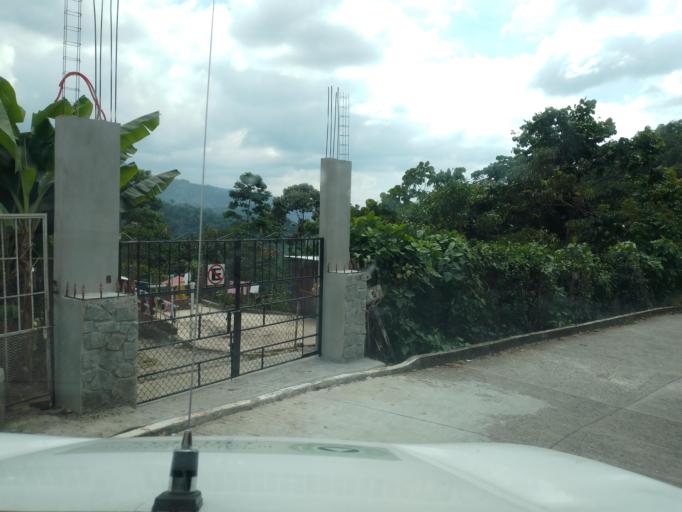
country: MX
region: Chiapas
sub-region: Union Juarez
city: Santo Domingo
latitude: 15.0581
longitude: -92.0928
